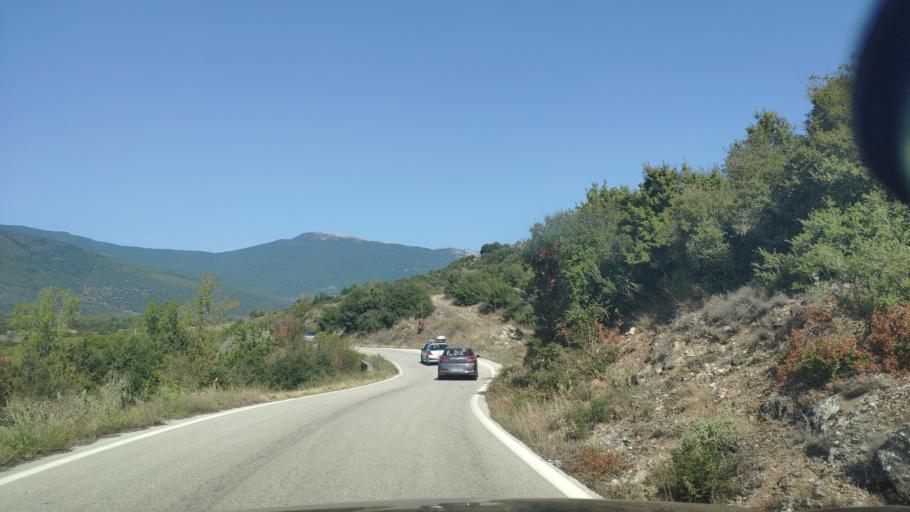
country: GR
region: West Greece
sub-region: Nomos Achaias
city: Aiyira
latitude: 37.8985
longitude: 22.3351
